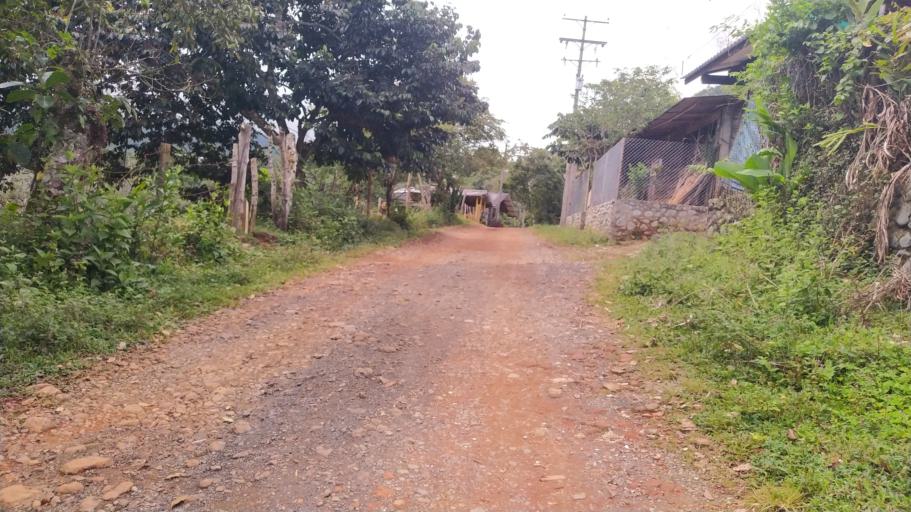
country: CO
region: Valle del Cauca
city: Cali
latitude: 3.4263
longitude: -76.6172
